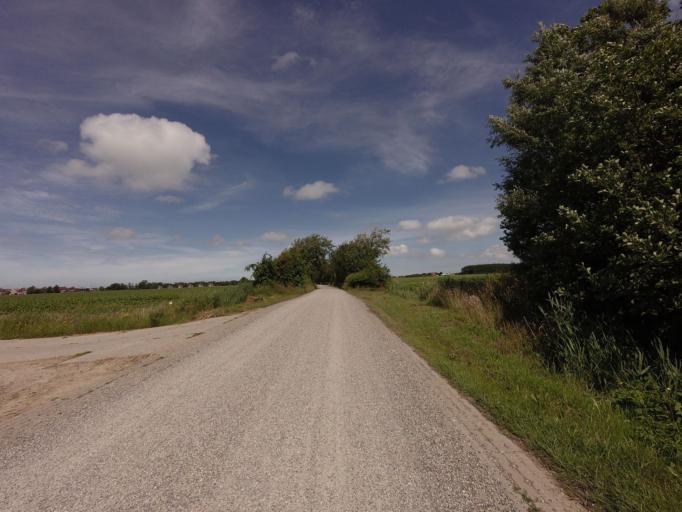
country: NL
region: North Holland
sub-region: Gemeente Texel
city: Den Burg
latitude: 53.0599
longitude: 4.8127
